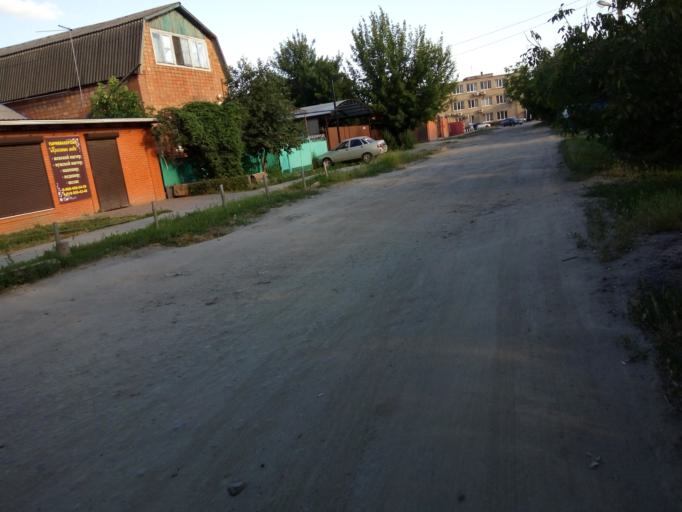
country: RU
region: Rostov
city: Bataysk
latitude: 47.1161
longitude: 39.7356
